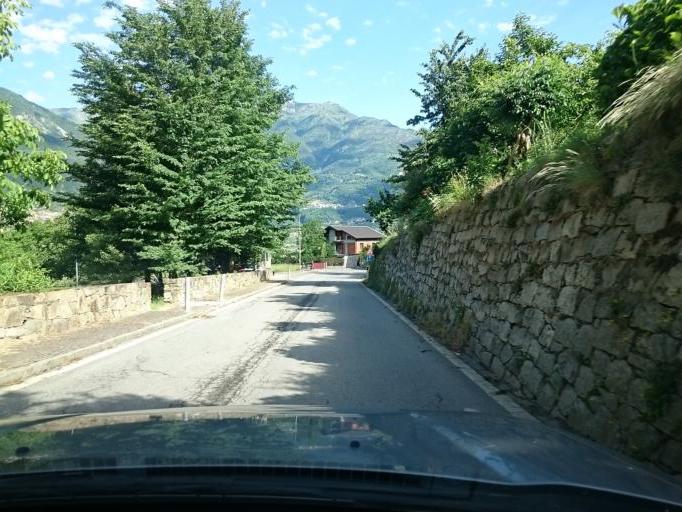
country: IT
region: Lombardy
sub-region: Provincia di Brescia
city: Ceto
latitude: 46.0090
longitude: 10.3528
